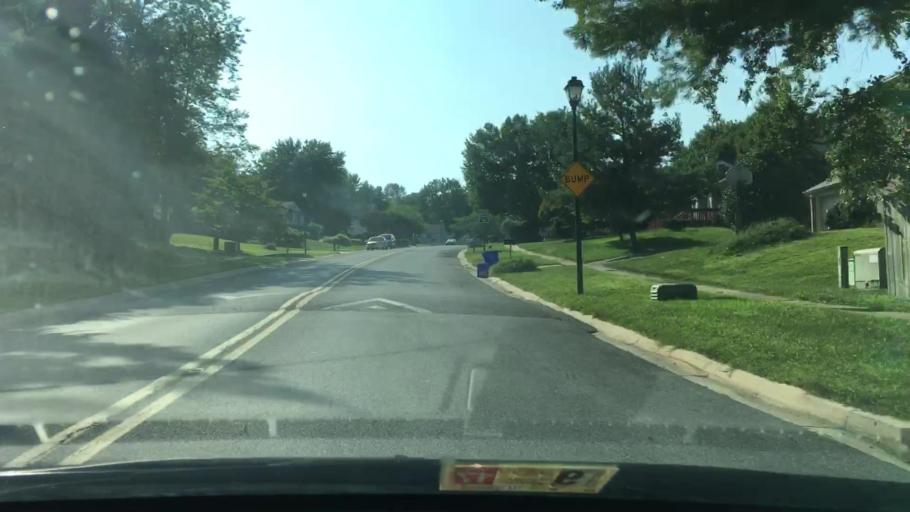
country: US
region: Maryland
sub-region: Montgomery County
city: Damascus
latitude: 39.2598
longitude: -77.2139
